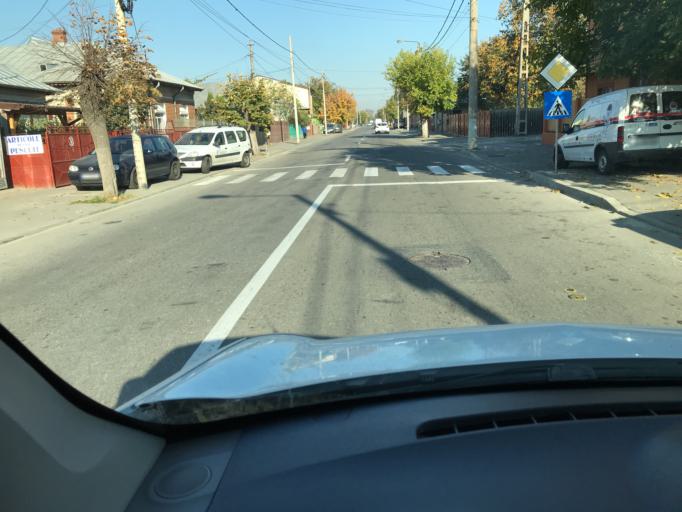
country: RO
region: Olt
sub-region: Municipiul Slatina
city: Slatina
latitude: 44.4339
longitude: 24.3510
